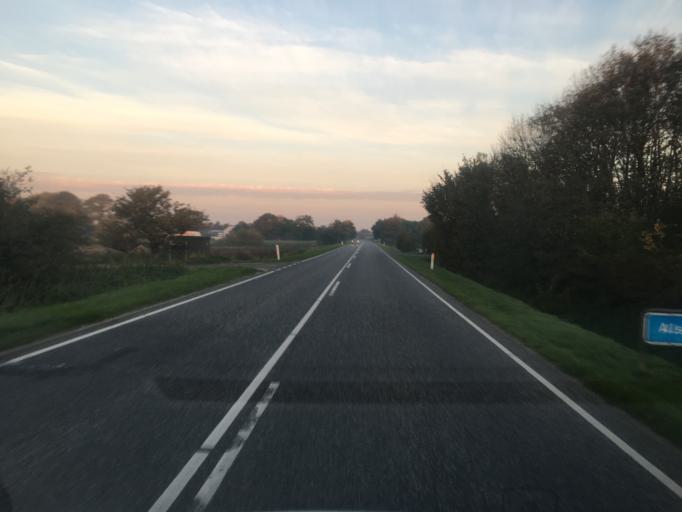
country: DK
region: South Denmark
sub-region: Tonder Kommune
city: Logumkloster
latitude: 55.0312
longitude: 9.0497
